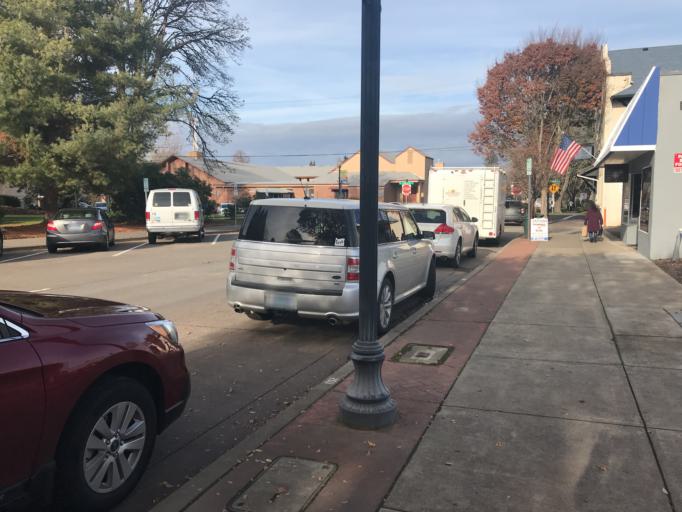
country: US
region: Oregon
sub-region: Washington County
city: Hillsboro
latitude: 45.5234
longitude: -122.9879
